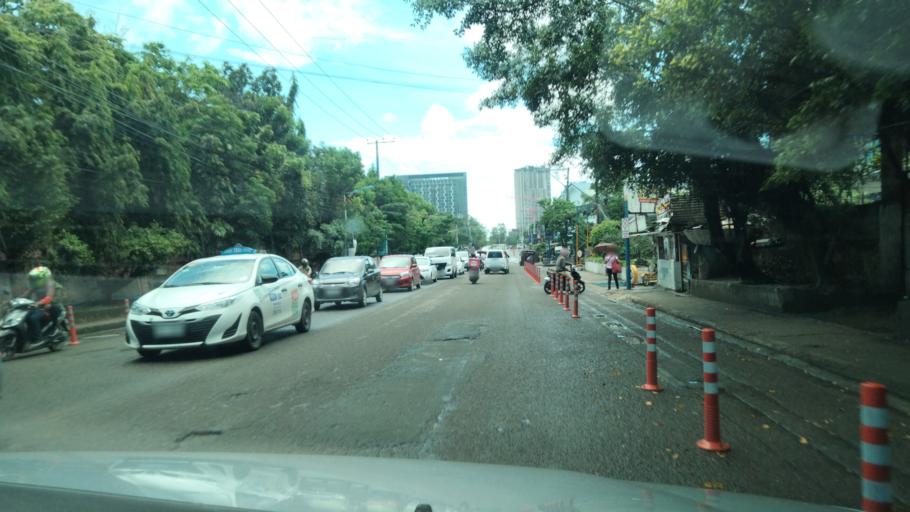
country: PH
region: Central Visayas
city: Mandaue City
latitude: 10.3291
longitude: 123.9328
